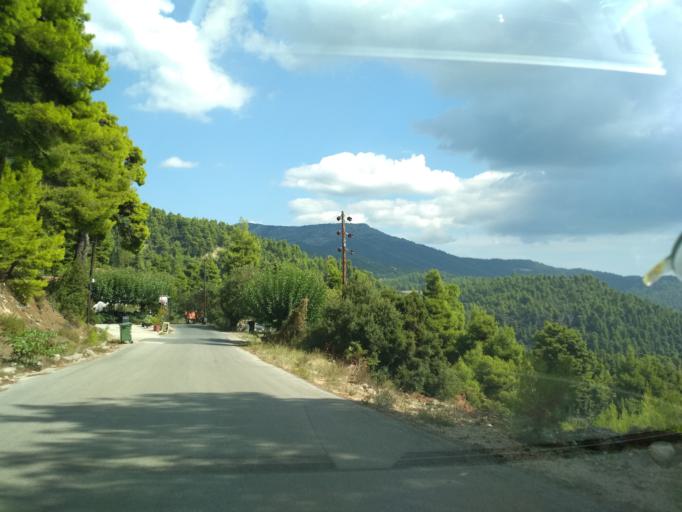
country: GR
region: Central Greece
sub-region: Nomos Evvoias
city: Roviai
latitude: 38.8253
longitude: 23.2801
